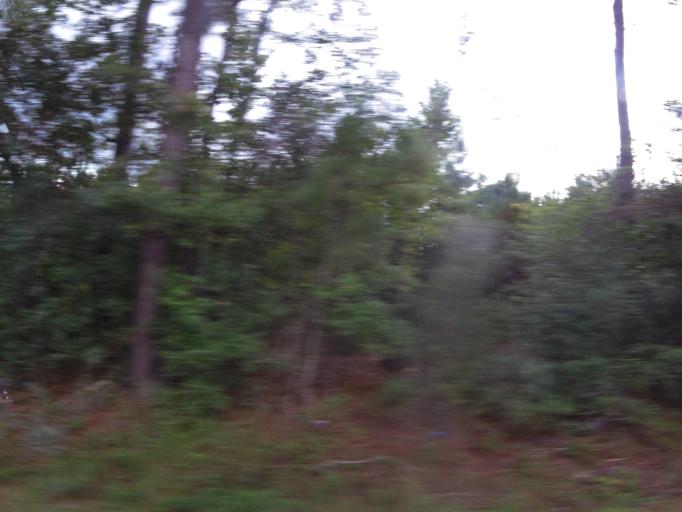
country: US
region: Georgia
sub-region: Liberty County
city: Midway
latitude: 31.8559
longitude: -81.4263
